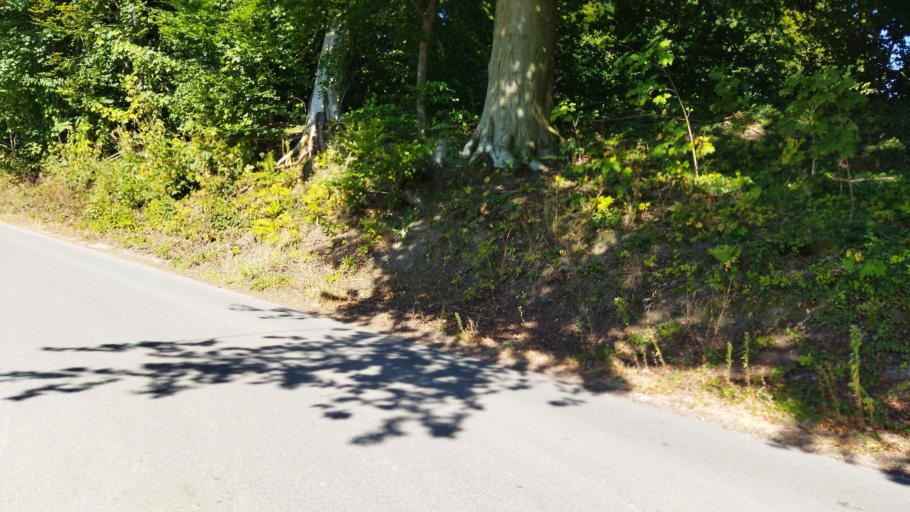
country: DE
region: North Rhine-Westphalia
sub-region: Regierungsbezirk Munster
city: Tecklenburg
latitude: 52.2137
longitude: 7.8138
